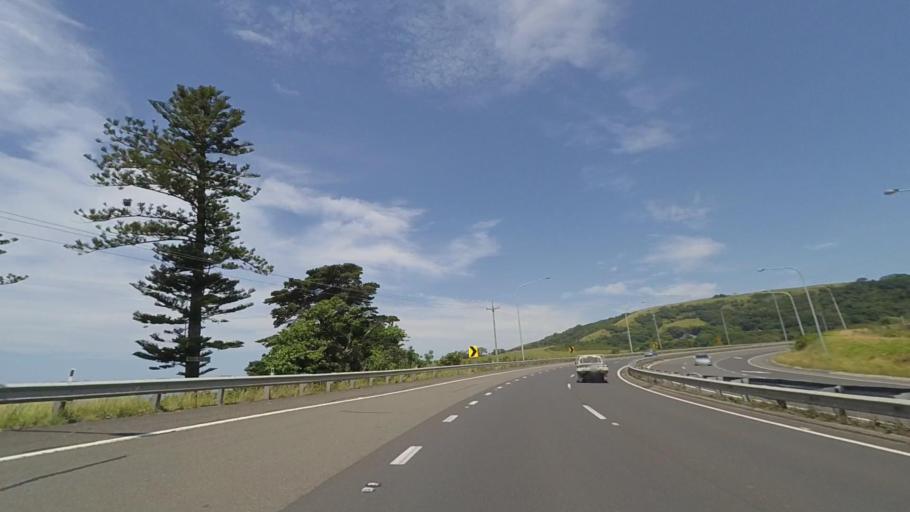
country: AU
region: New South Wales
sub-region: Kiama
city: Kiama
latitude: -34.6978
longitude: 150.8436
